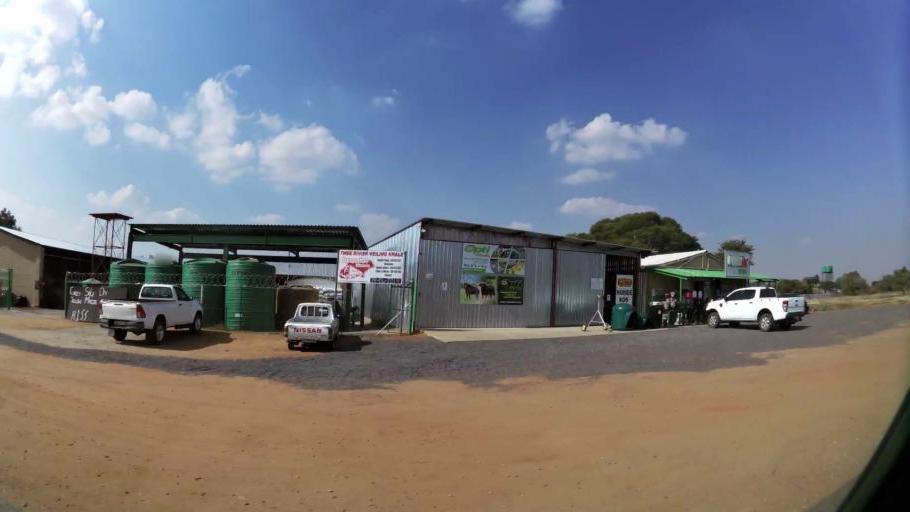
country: ZA
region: North-West
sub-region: Bojanala Platinum District Municipality
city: Rustenburg
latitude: -25.4881
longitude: 27.0859
